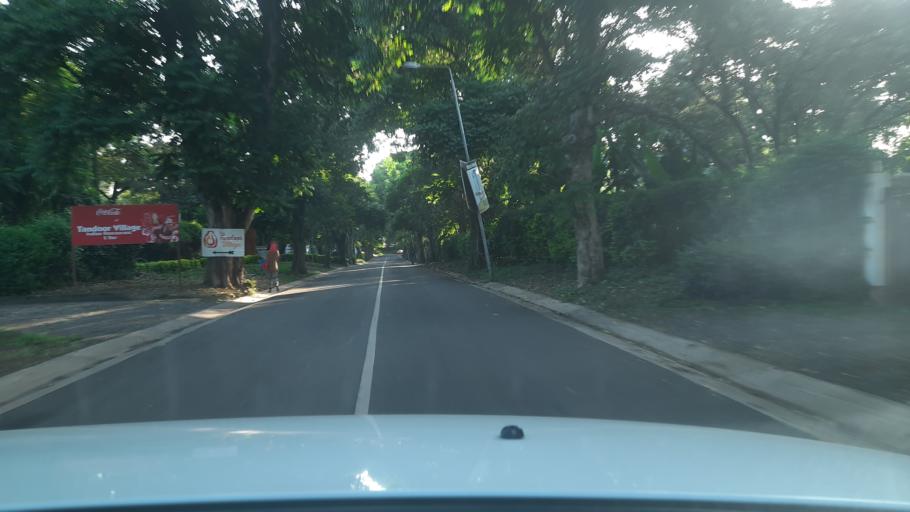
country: TZ
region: Arusha
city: Arusha
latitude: -3.3793
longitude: 36.6993
